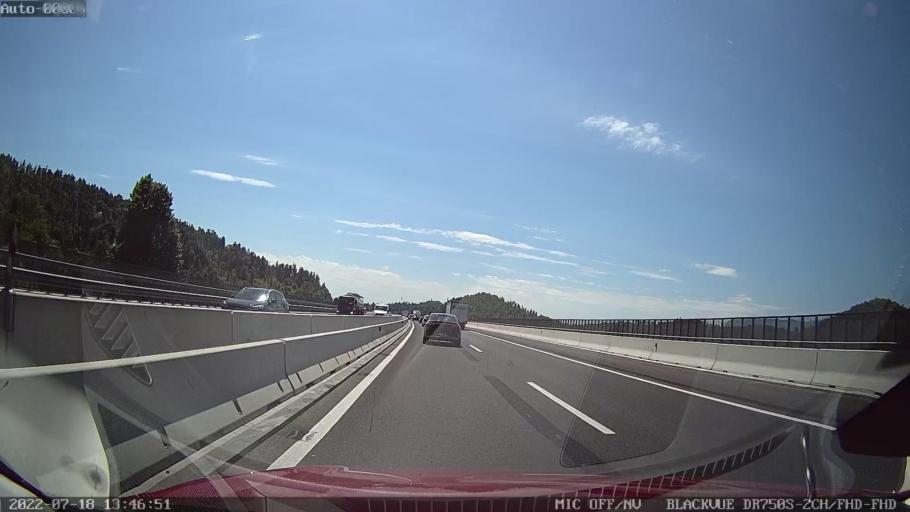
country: SI
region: Postojna
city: Postojna
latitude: 45.7920
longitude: 14.2270
